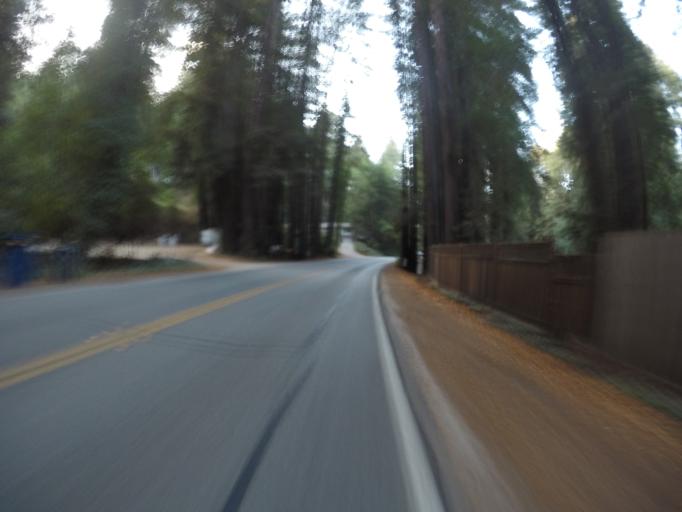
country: US
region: California
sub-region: Santa Cruz County
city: Mount Hermon
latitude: 37.0354
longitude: -122.0648
